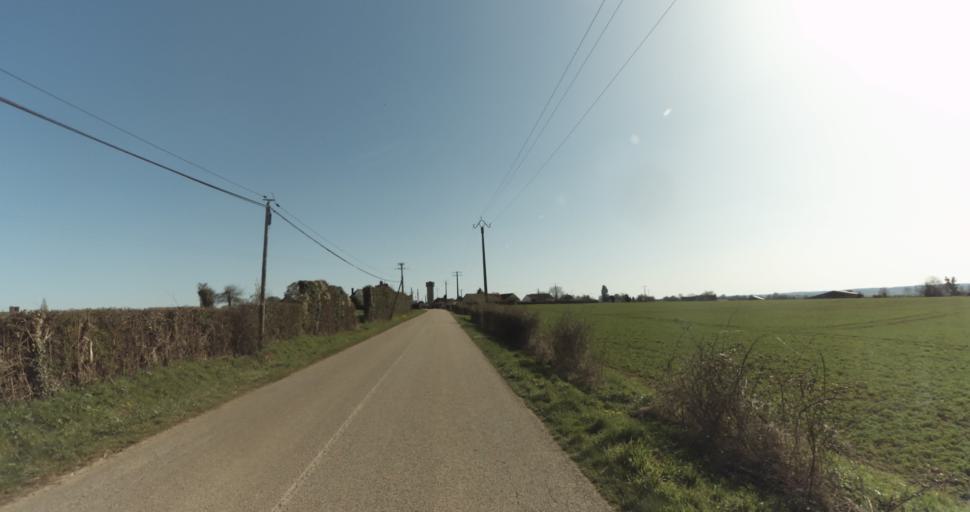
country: FR
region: Lower Normandy
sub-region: Departement de l'Orne
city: Trun
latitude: 48.8741
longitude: 0.0294
